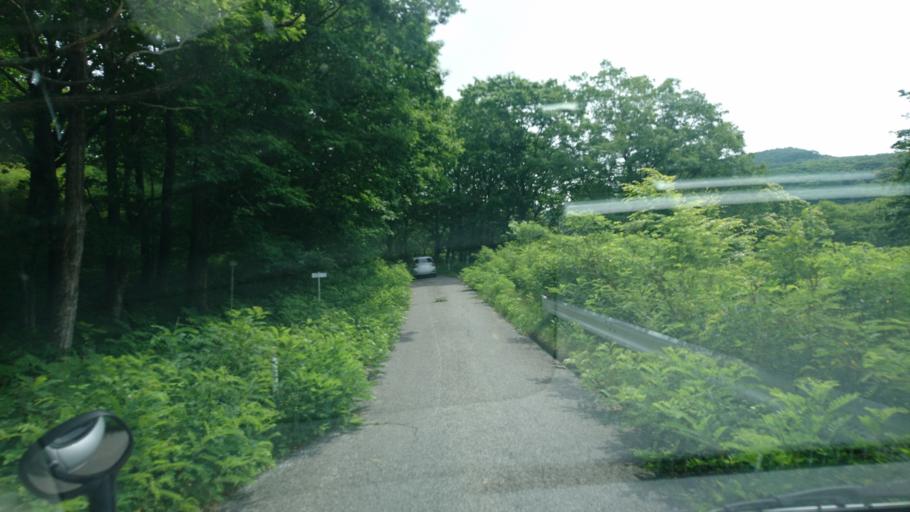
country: JP
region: Iwate
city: Ofunato
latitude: 39.1750
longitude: 141.7792
